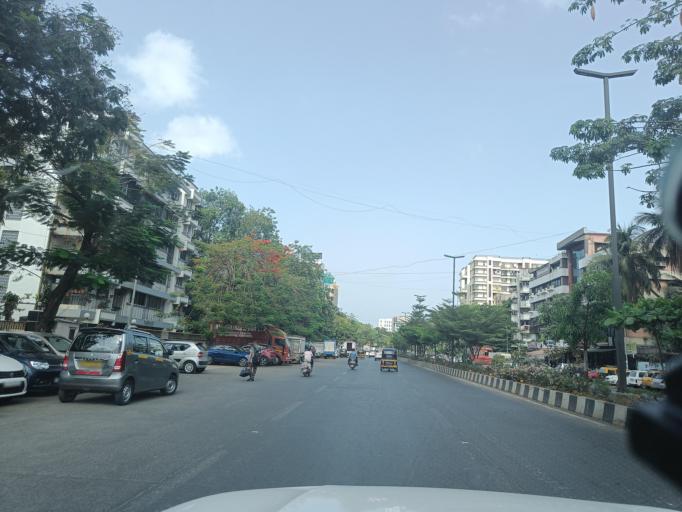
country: IN
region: Maharashtra
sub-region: Mumbai Suburban
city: Powai
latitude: 19.1113
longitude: 72.8645
